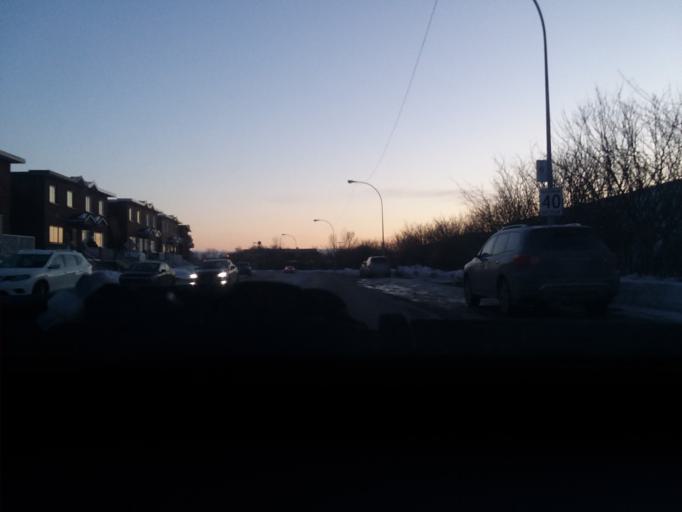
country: CA
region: Quebec
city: Montreal-Ouest
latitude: 45.4374
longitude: -73.6356
